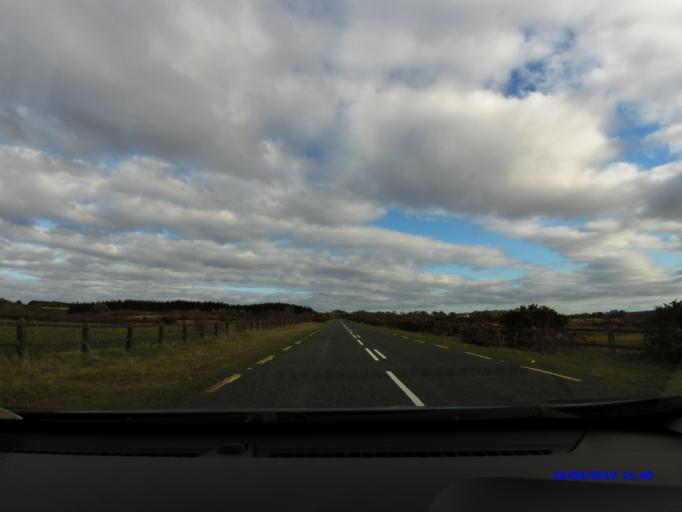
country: IE
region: Connaught
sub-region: Maigh Eo
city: Ballyhaunis
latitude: 53.8818
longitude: -8.7900
